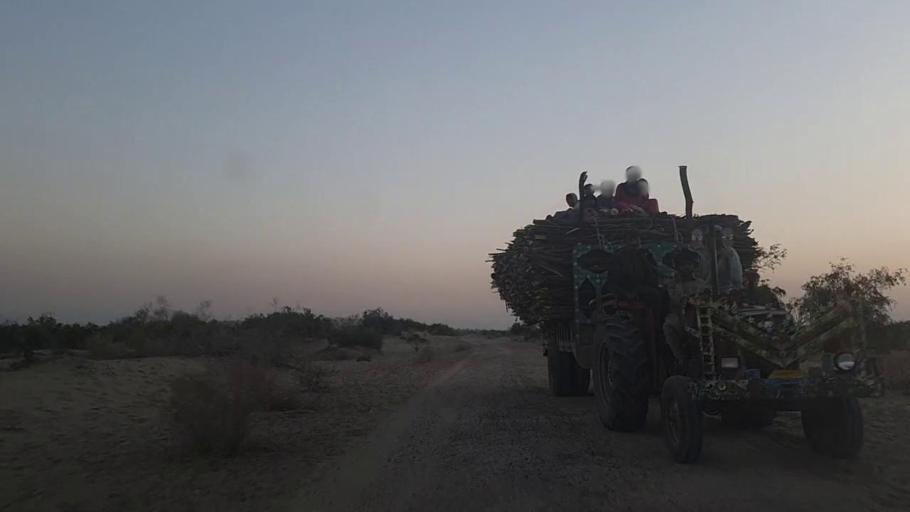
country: PK
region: Sindh
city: Jam Sahib
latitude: 26.4072
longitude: 68.8096
